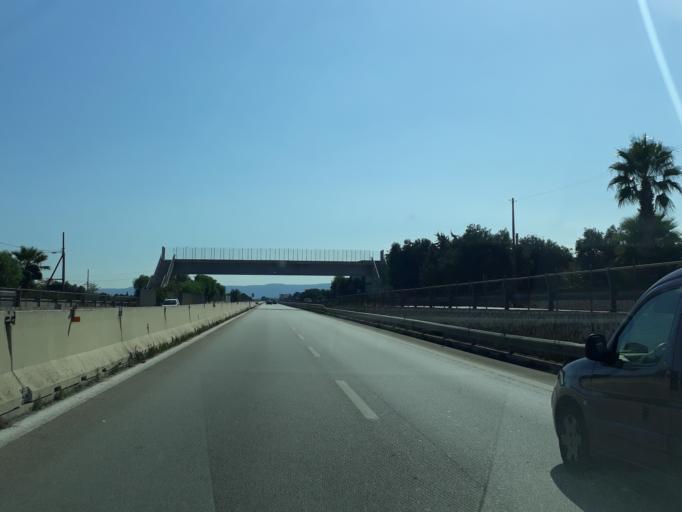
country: IT
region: Apulia
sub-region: Provincia di Brindisi
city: Fasano
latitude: 40.8690
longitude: 17.3441
